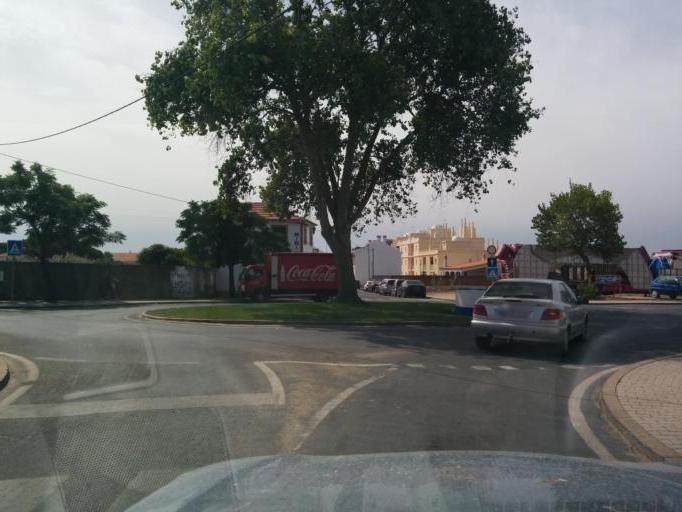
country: PT
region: Beja
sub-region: Odemira
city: Vila Nova de Milfontes
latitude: 37.7258
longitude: -8.7842
